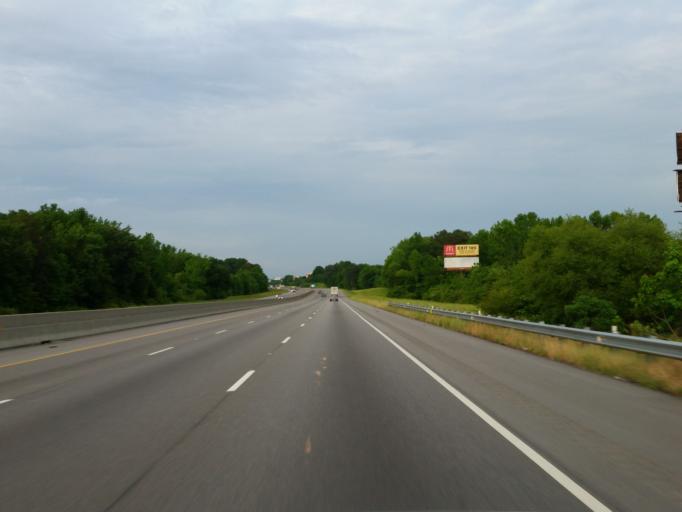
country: US
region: Alabama
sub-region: Calhoun County
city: Oxford
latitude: 33.5922
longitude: -85.8615
